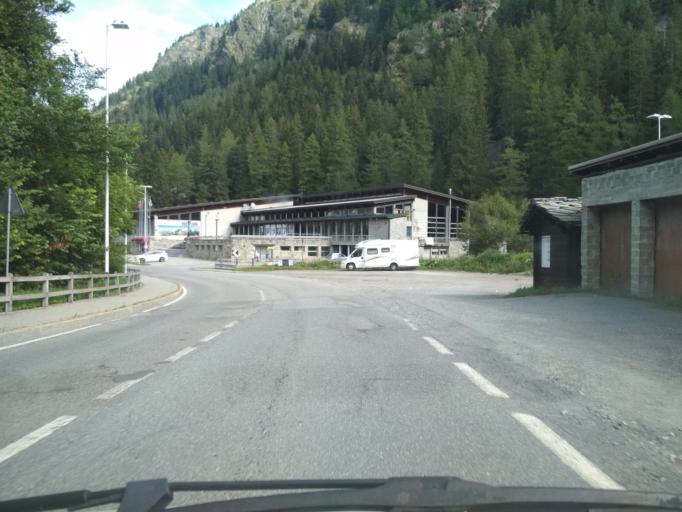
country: IT
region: Aosta Valley
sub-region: Valle d'Aosta
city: Gressoney-Saint-Jean
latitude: 45.7654
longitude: 7.8357
